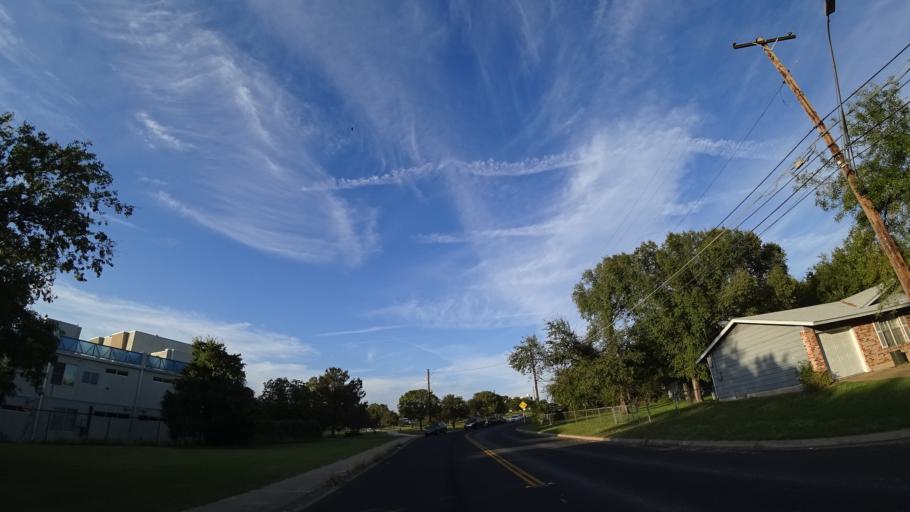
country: US
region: Texas
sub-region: Travis County
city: Austin
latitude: 30.2128
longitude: -97.7676
